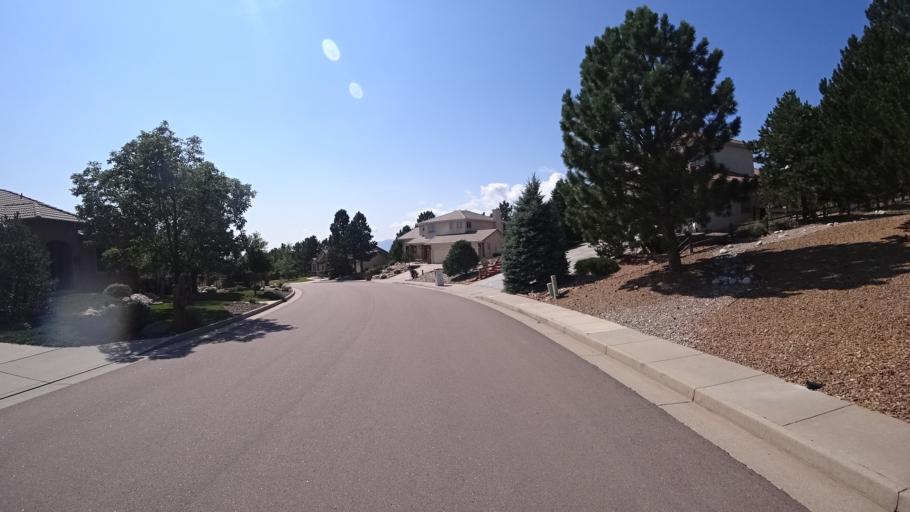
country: US
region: Colorado
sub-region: El Paso County
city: Manitou Springs
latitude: 38.9203
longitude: -104.8808
